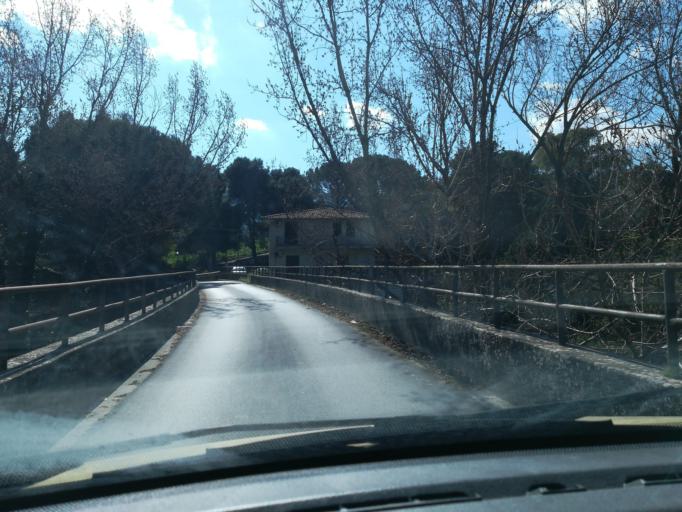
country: IT
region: Sicily
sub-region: Palermo
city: Cannizzaro-Favara
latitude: 38.0511
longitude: 13.2591
